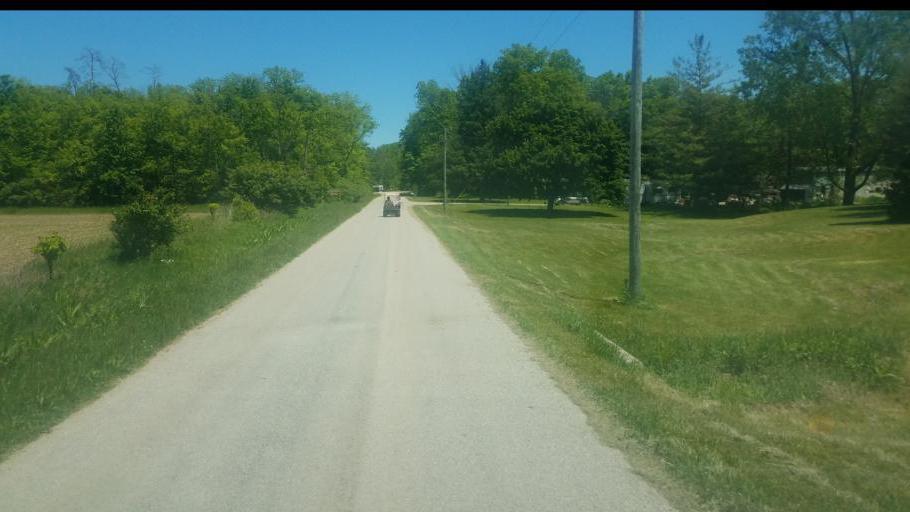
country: US
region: Ohio
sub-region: Miami County
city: Piqua
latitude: 40.2160
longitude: -84.2606
